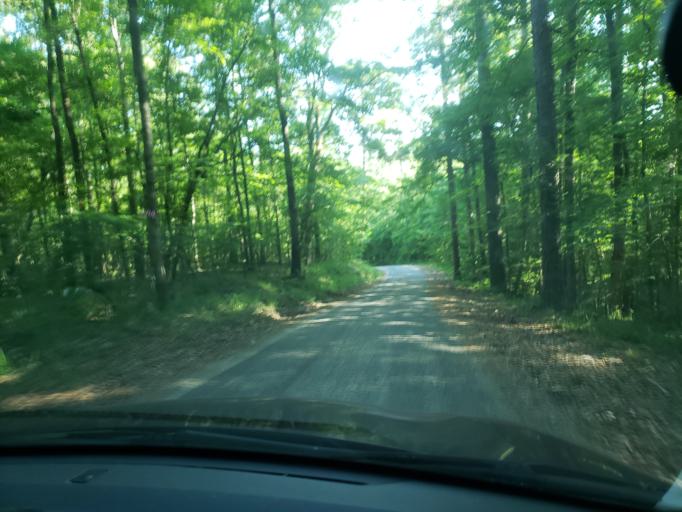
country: US
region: Alabama
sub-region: Elmore County
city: Tallassee
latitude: 32.5961
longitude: -85.8773
